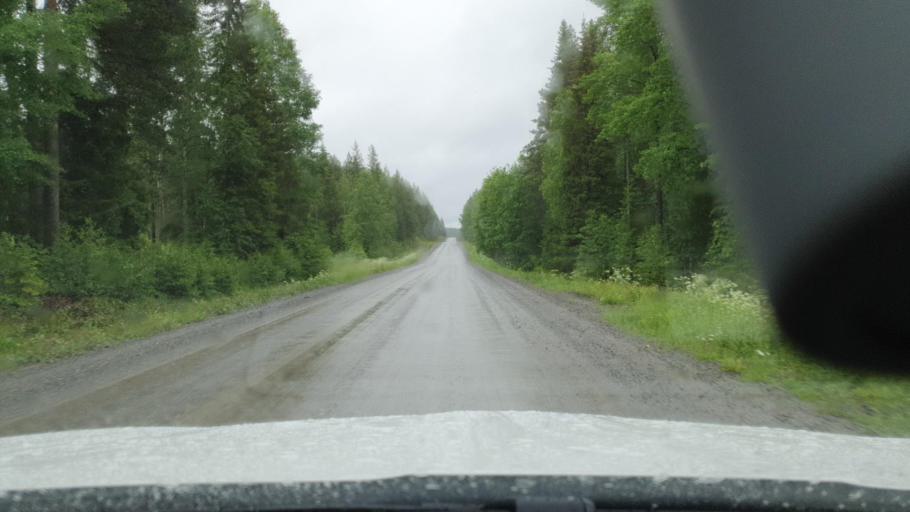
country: SE
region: Vaesterbotten
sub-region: Skelleftea Kommun
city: Burtraesk
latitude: 64.3824
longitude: 20.3243
